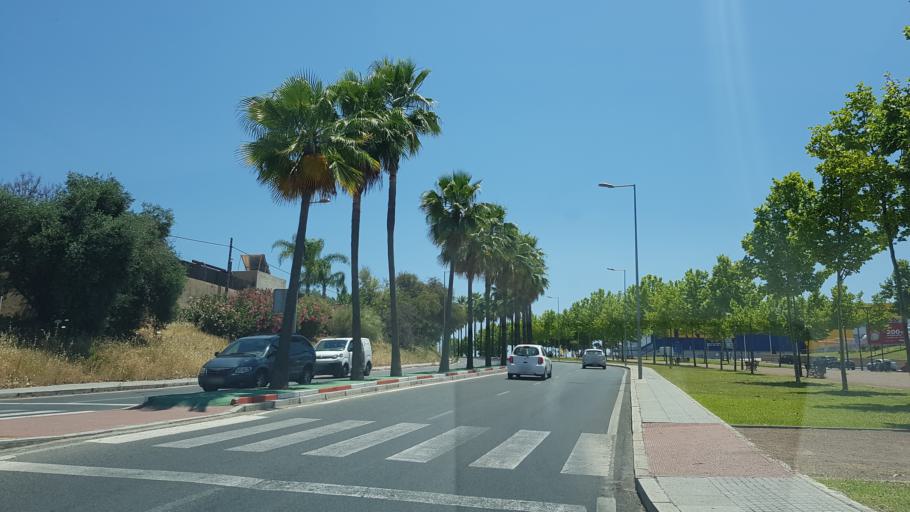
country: ES
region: Andalusia
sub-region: Provincia de Sevilla
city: Castilleja de la Cuesta
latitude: 37.3860
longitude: -6.0460
